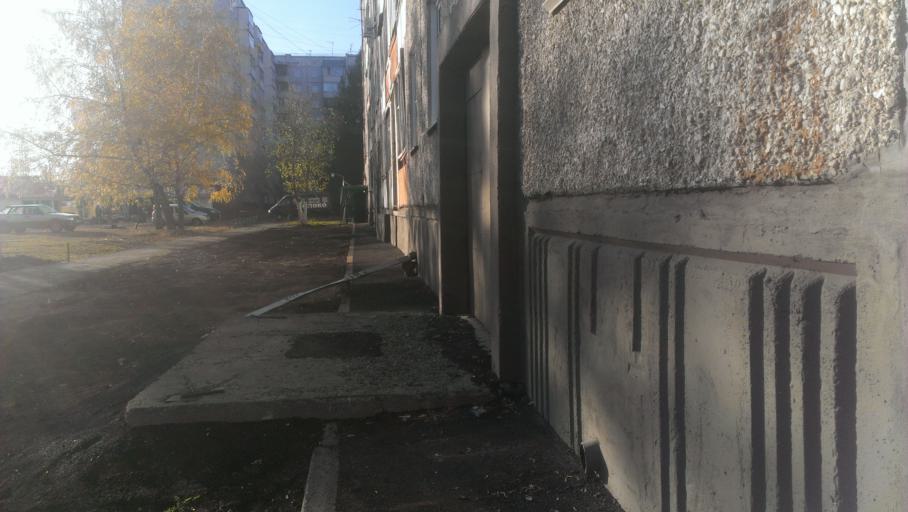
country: RU
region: Altai Krai
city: Novosilikatnyy
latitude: 53.3563
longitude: 83.6770
